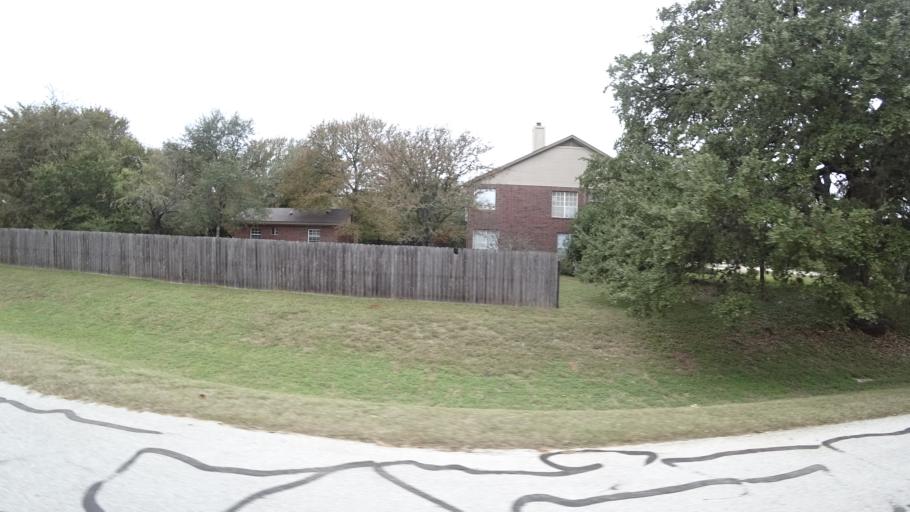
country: US
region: Texas
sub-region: Travis County
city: Shady Hollow
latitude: 30.1578
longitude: -97.8682
